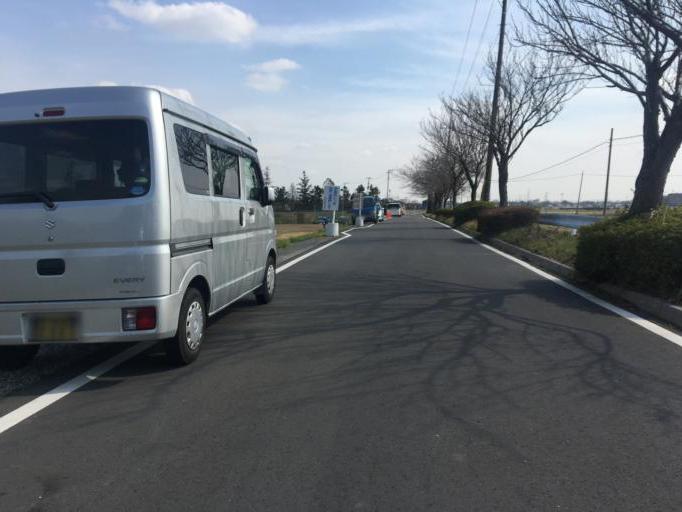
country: JP
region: Saitama
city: Oi
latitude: 35.8734
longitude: 139.5589
